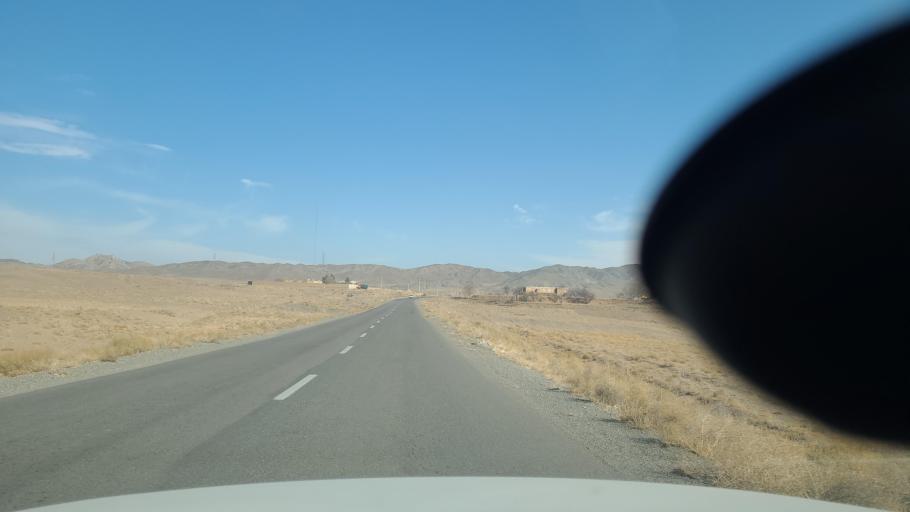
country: IR
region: Razavi Khorasan
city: Fariman
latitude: 35.5948
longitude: 59.6934
